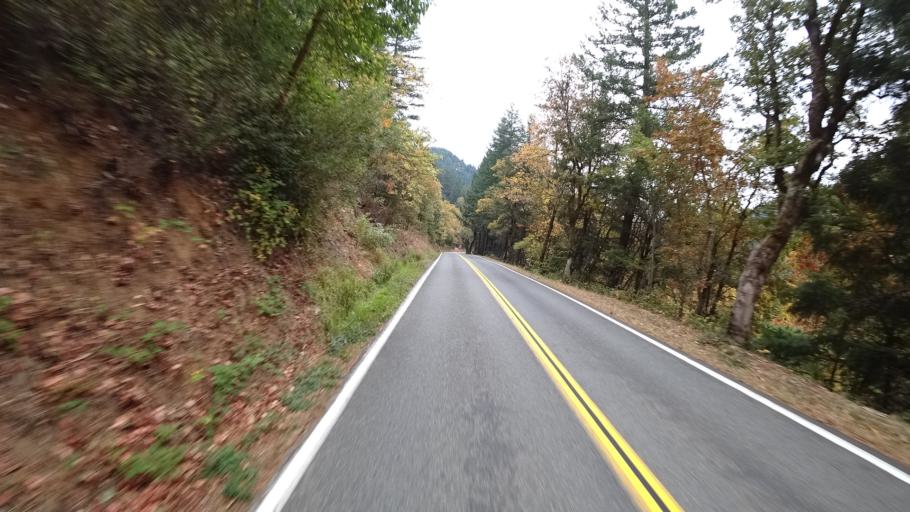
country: US
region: California
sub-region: Siskiyou County
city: Happy Camp
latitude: 41.8558
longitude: -123.3906
